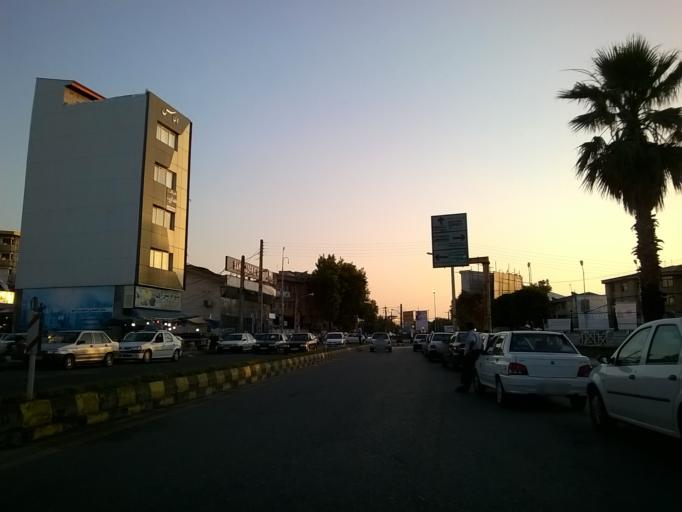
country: IR
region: Gilan
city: Astaneh-ye Ashrafiyeh
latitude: 37.2660
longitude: 49.9439
